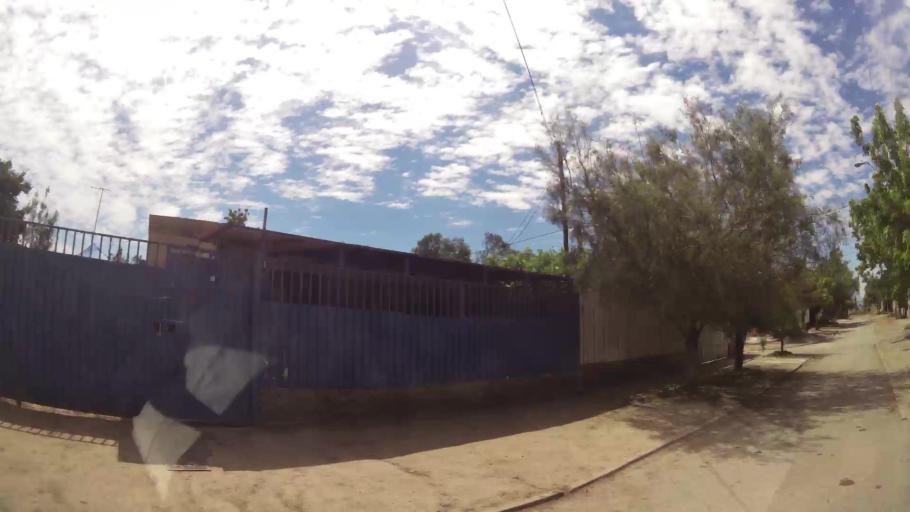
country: CL
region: Santiago Metropolitan
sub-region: Provincia de Santiago
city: La Pintana
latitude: -33.5733
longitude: -70.6592
